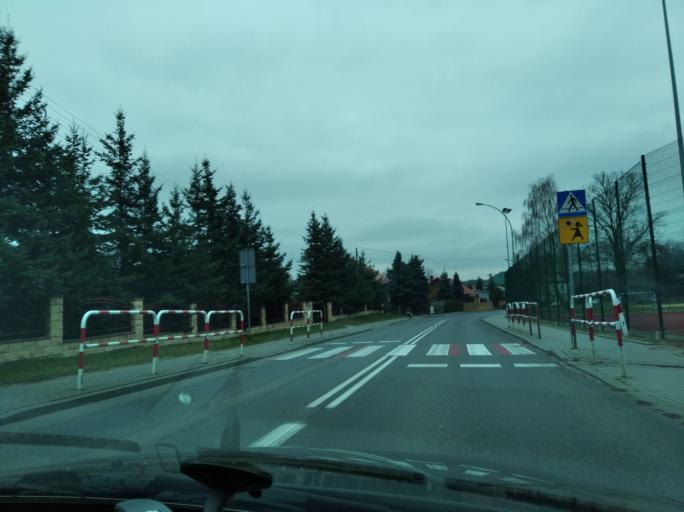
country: PL
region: Subcarpathian Voivodeship
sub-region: Powiat lancucki
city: Zolynia
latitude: 50.1647
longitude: 22.3096
